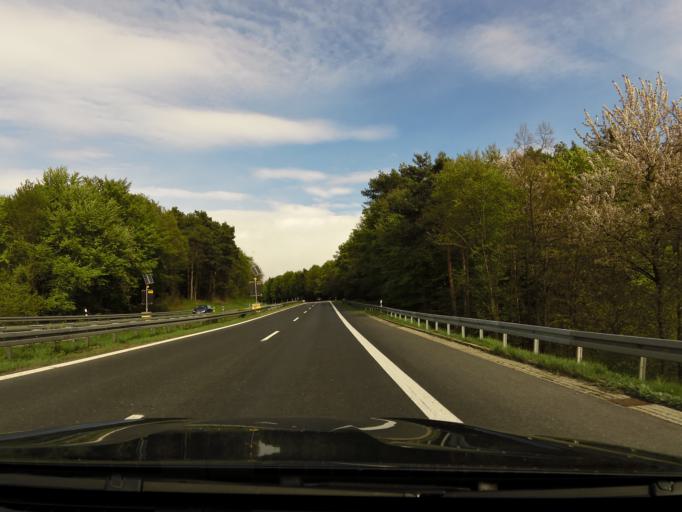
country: DE
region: Bavaria
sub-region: Upper Bavaria
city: Wolnzach
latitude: 48.6093
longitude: 11.6615
